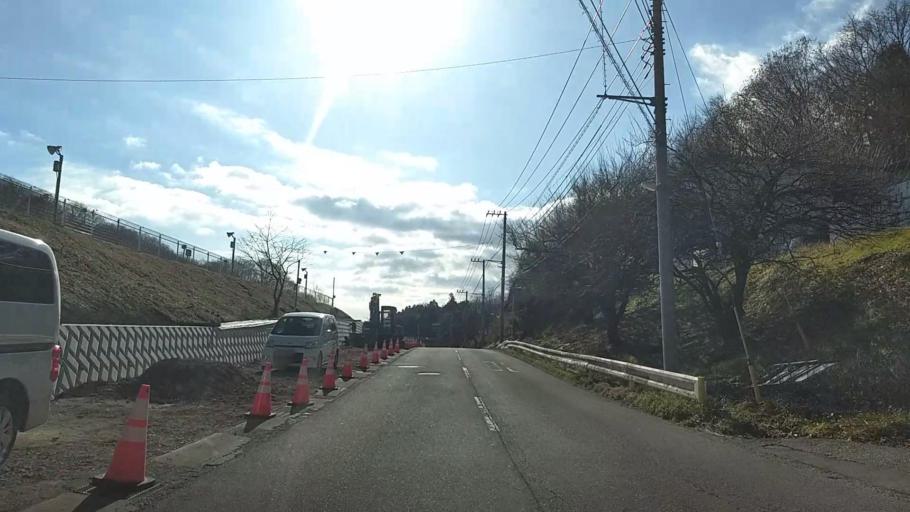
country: JP
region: Kanagawa
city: Atsugi
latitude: 35.4667
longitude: 139.2883
